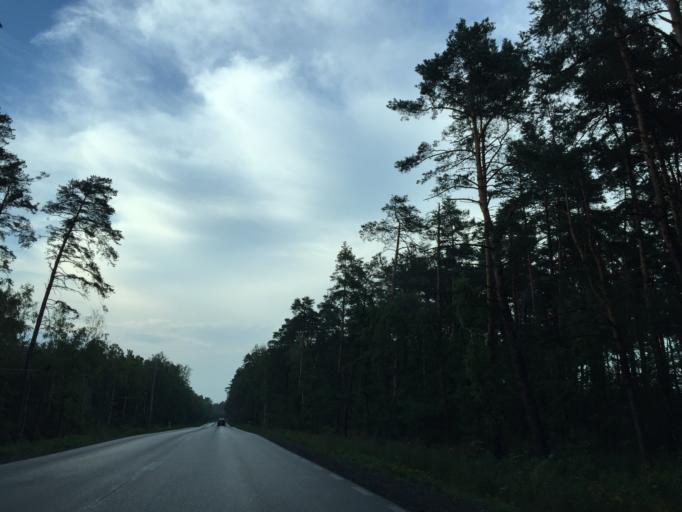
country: PL
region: Masovian Voivodeship
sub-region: Powiat wegrowski
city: Sadowne
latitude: 52.6222
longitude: 21.8424
